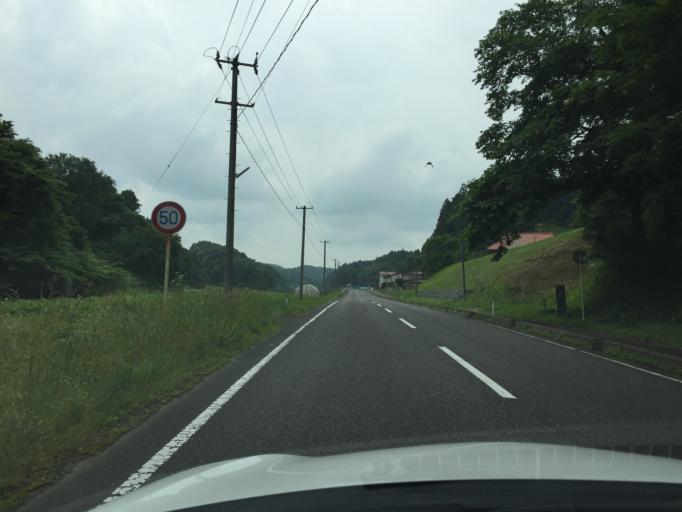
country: JP
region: Fukushima
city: Funehikimachi-funehiki
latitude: 37.2907
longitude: 140.5885
